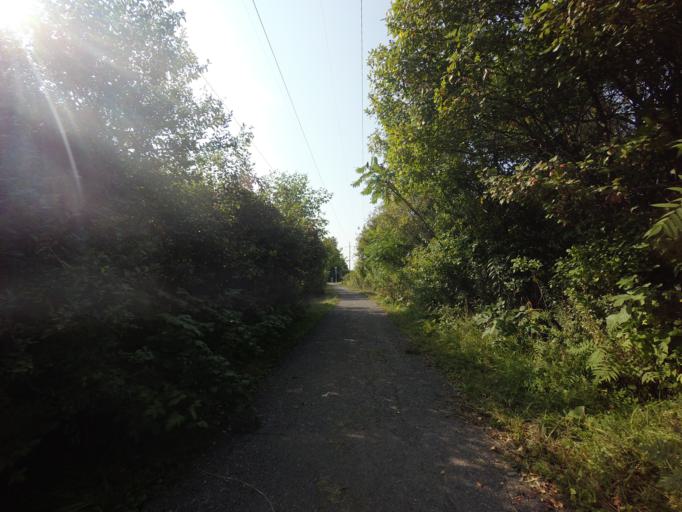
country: CA
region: Ontario
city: Bells Corners
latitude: 45.2914
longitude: -75.8485
